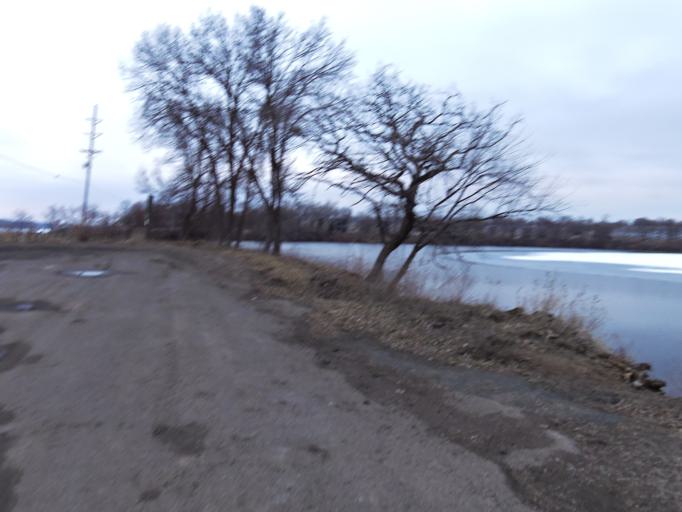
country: US
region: Wisconsin
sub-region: Saint Croix County
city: North Hudson
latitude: 44.9875
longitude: -92.7624
